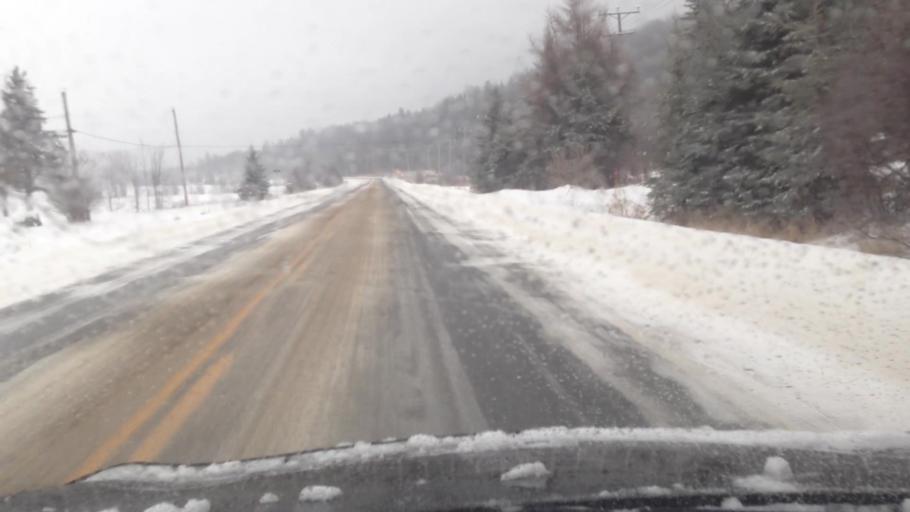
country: CA
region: Quebec
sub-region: Laurentides
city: Mont-Tremblant
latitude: 46.0631
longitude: -74.6216
